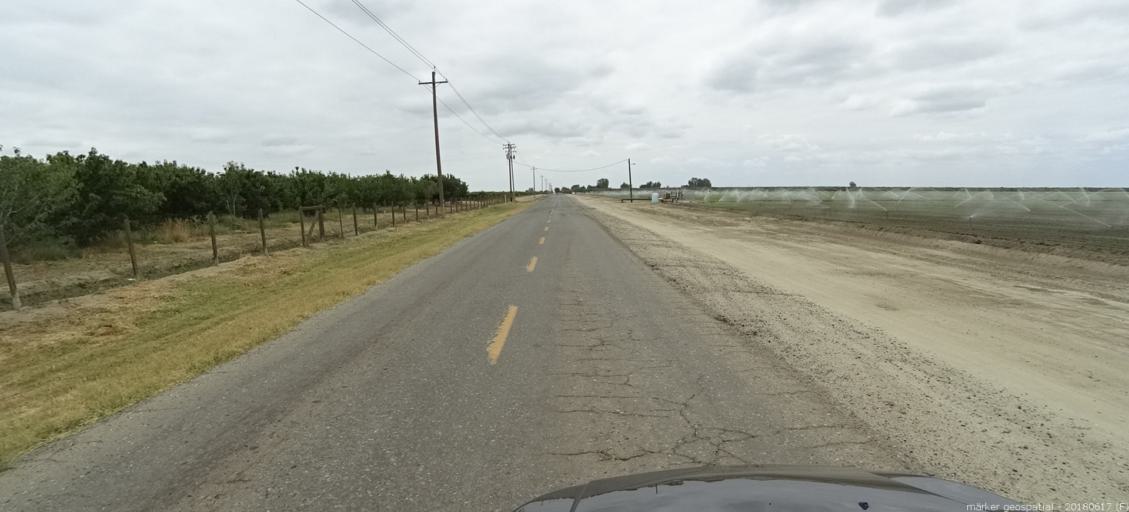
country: US
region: California
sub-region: Madera County
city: Madera
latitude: 36.9141
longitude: -120.1652
